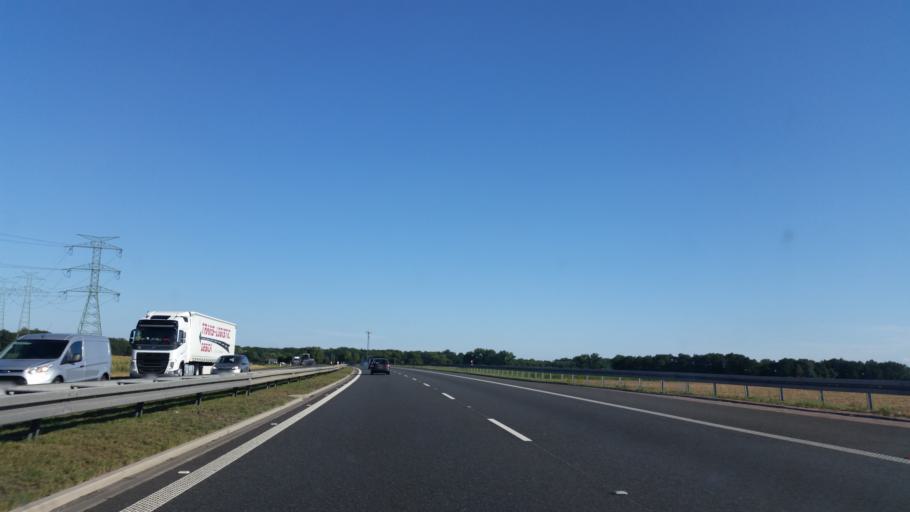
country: PL
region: Lower Silesian Voivodeship
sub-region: Powiat strzelinski
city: Wiazow
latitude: 50.8551
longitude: 17.2289
